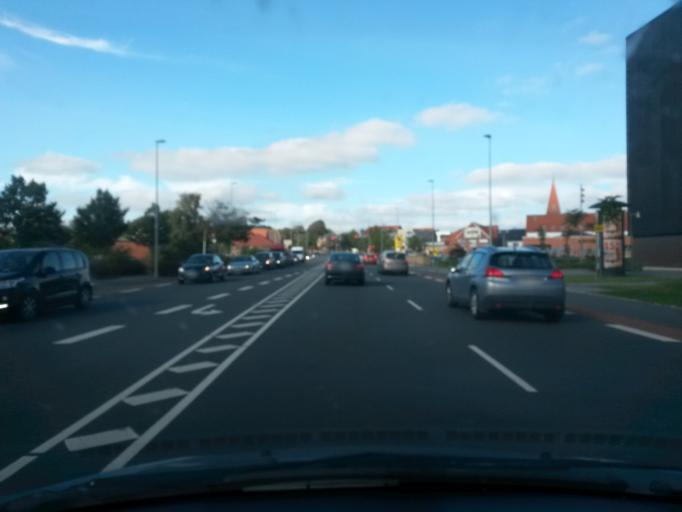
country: DK
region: Central Jutland
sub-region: Holstebro Kommune
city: Holstebro
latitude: 56.3562
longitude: 8.6151
